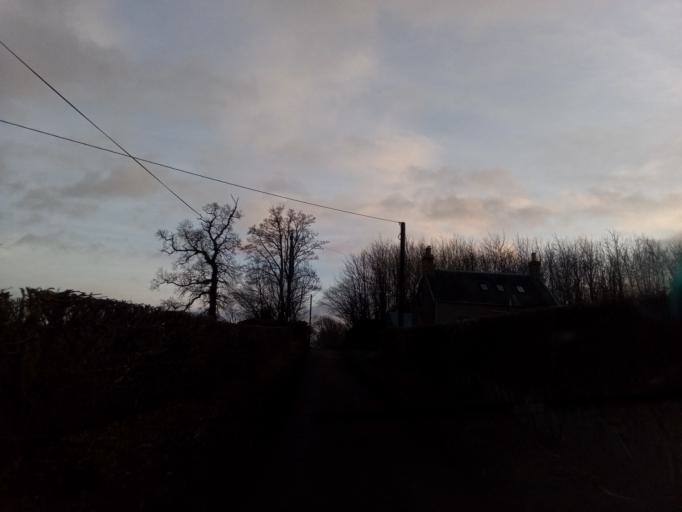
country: GB
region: Scotland
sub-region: The Scottish Borders
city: Newtown St Boswells
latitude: 55.5330
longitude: -2.7085
